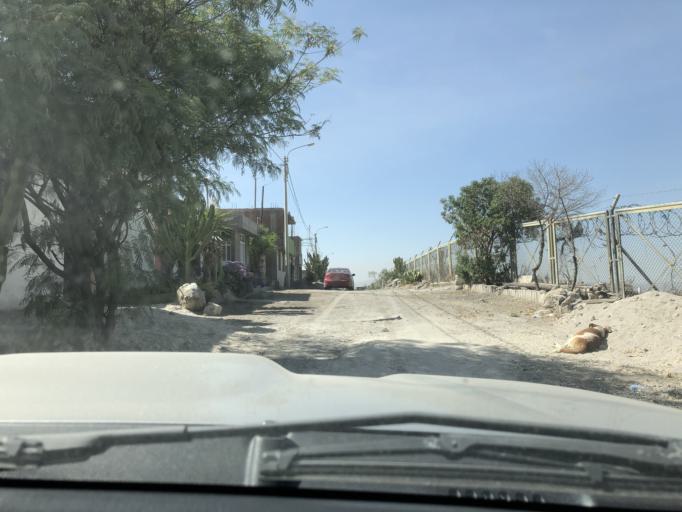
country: PE
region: Arequipa
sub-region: Provincia de Arequipa
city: Arequipa
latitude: -16.3412
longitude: -71.5524
